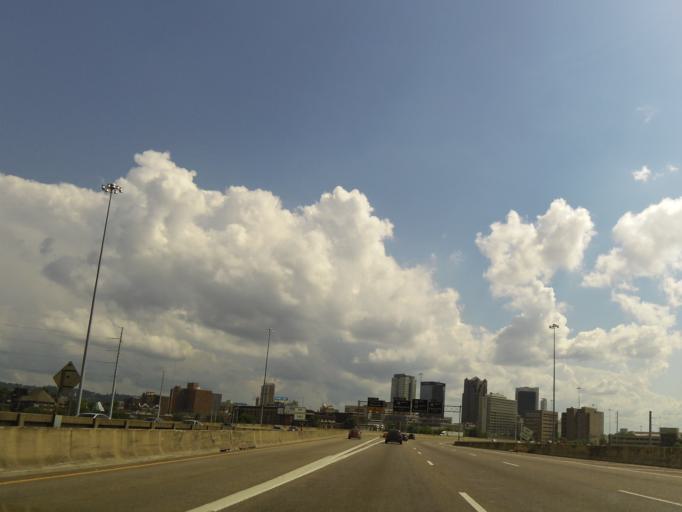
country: US
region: Alabama
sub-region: Jefferson County
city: Birmingham
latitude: 33.5277
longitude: -86.8046
